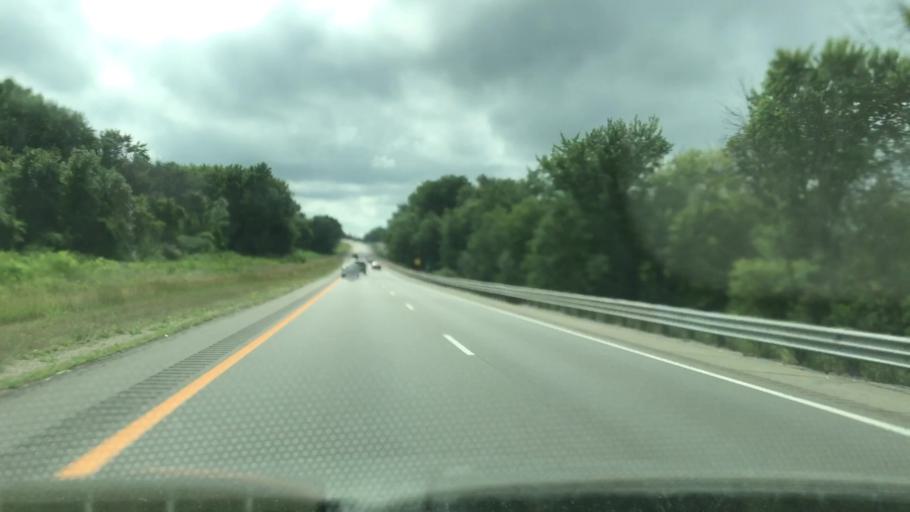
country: US
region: Michigan
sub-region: Ottawa County
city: Coopersville
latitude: 43.0744
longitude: -86.0475
